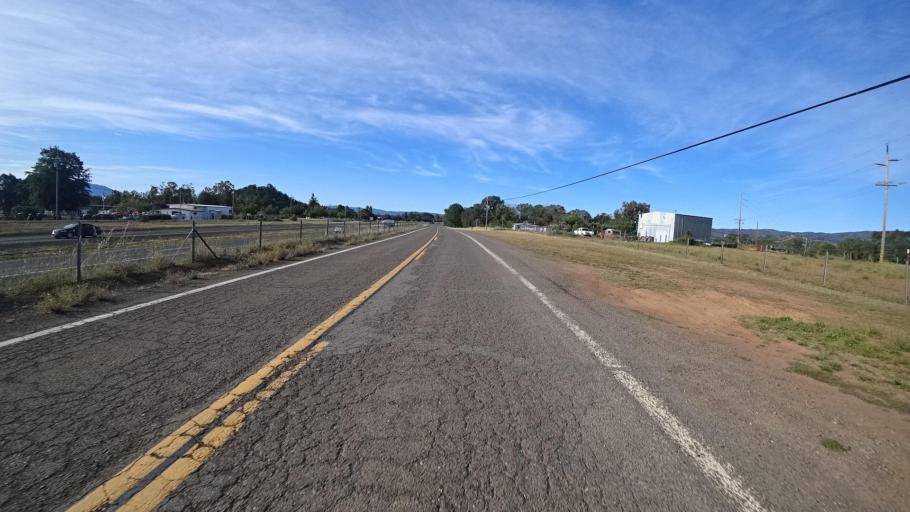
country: US
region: California
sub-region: Lake County
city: North Lakeport
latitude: 39.0784
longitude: -122.9312
